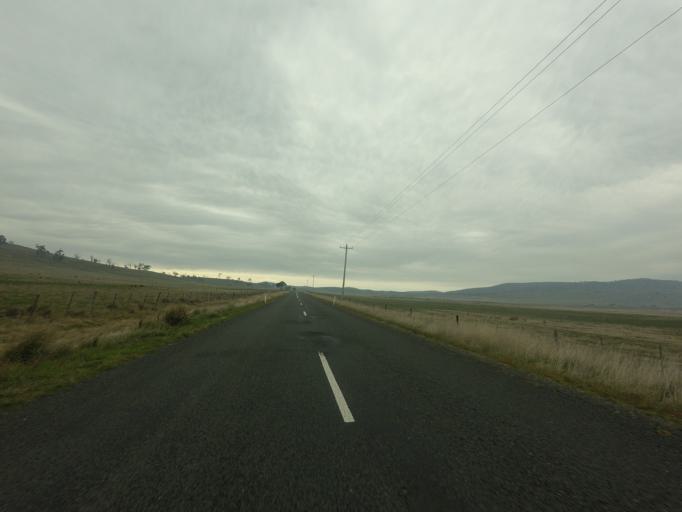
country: AU
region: Tasmania
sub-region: Derwent Valley
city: New Norfolk
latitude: -42.4413
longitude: 146.9771
